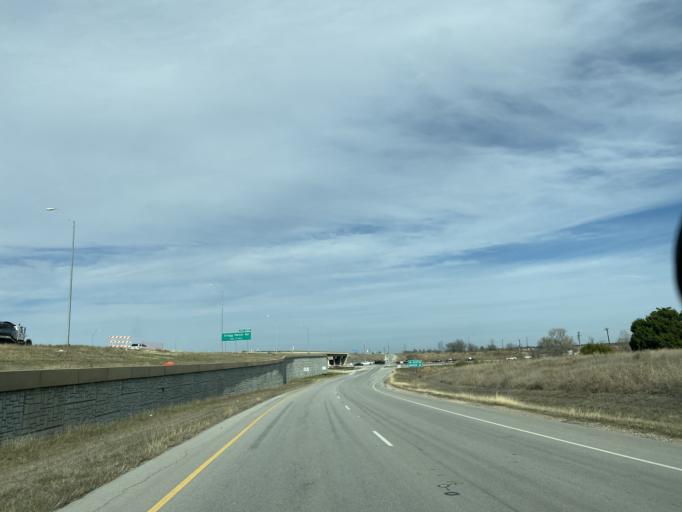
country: US
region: Texas
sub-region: Travis County
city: Manor
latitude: 30.3500
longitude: -97.5929
